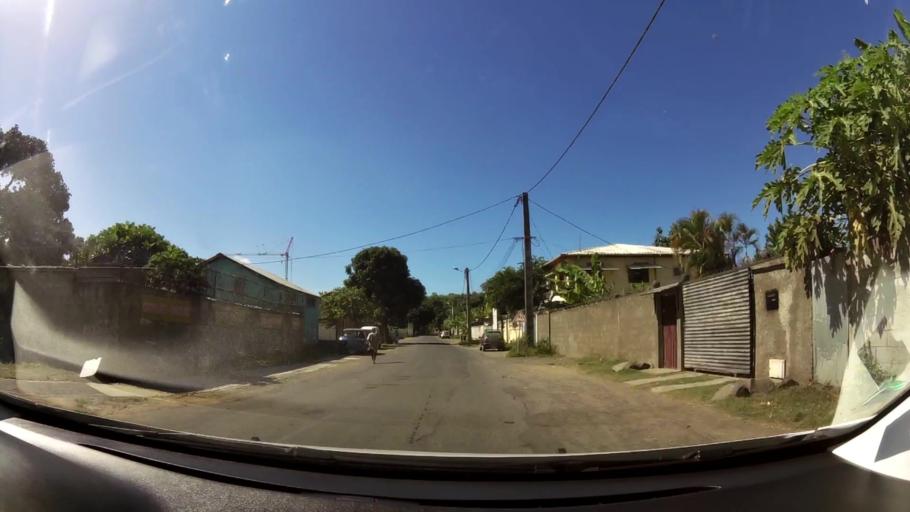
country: YT
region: Pamandzi
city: Pamandzi
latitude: -12.7809
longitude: 45.2797
